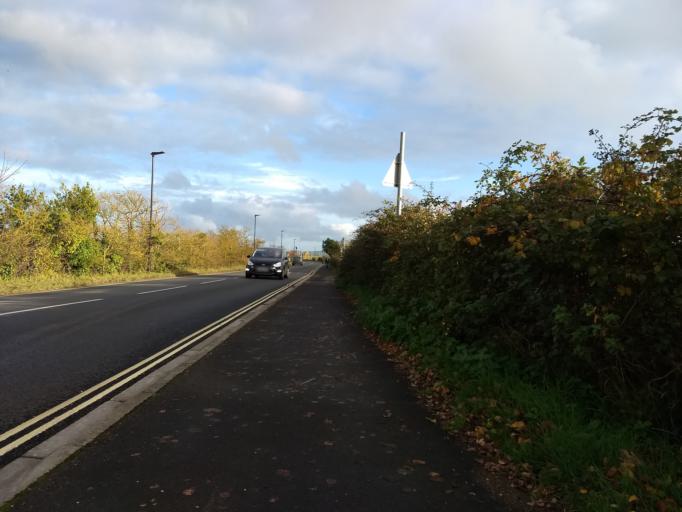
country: GB
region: England
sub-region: Isle of Wight
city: Yarmouth
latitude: 50.7050
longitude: -1.5090
